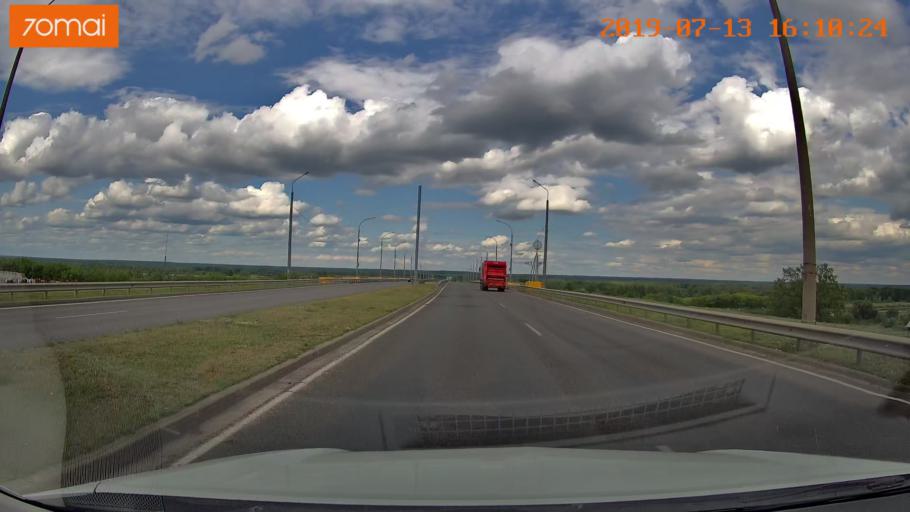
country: BY
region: Mogilev
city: Babruysk
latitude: 53.1606
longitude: 29.2397
